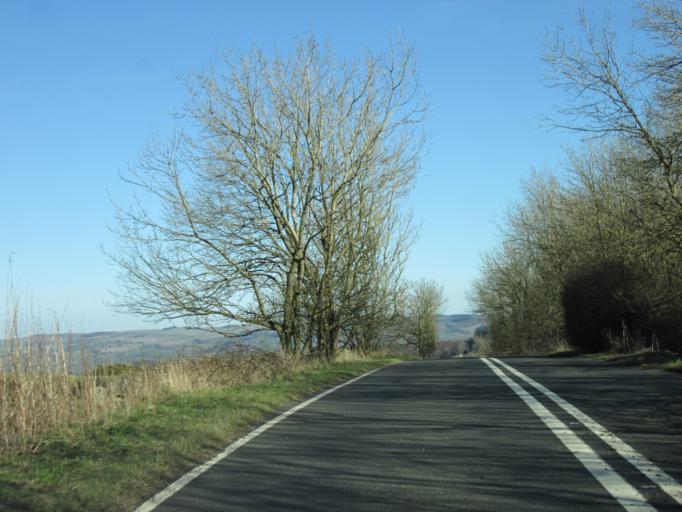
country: GB
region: England
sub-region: Northumberland
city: Birtley
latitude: 55.0382
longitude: -2.1938
